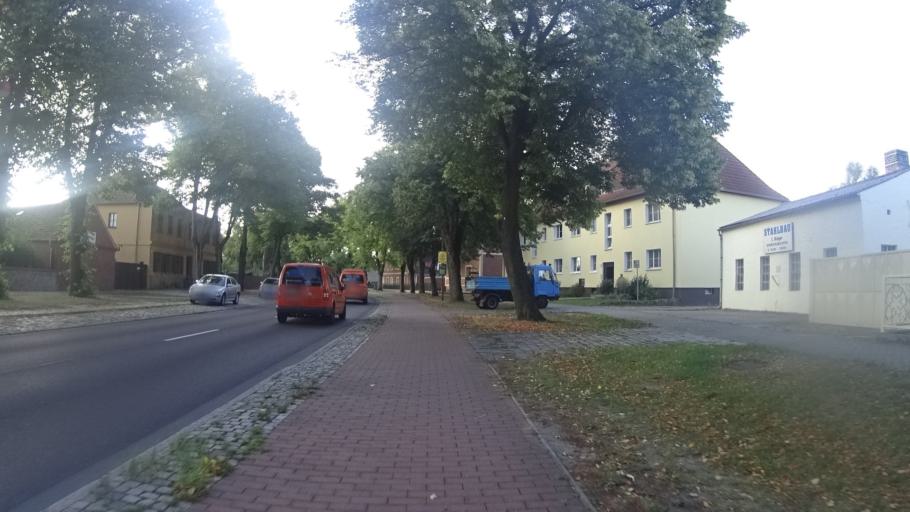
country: DE
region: Brandenburg
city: Premnitz
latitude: 52.5315
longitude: 12.3304
